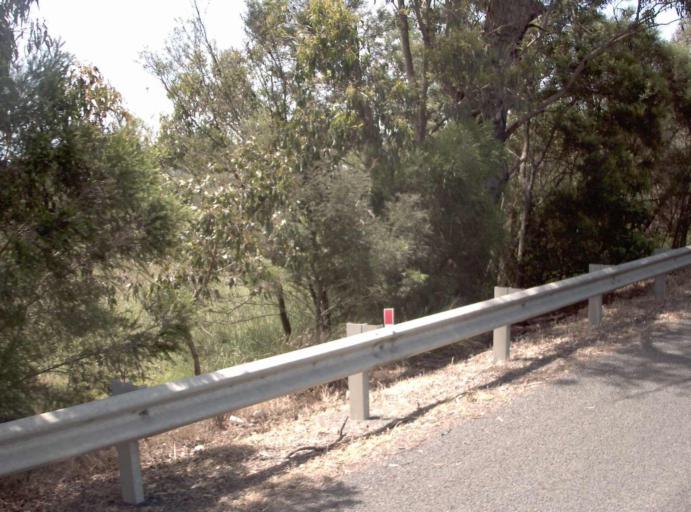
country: AU
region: Victoria
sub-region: Latrobe
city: Traralgon
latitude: -38.2104
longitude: 146.4889
